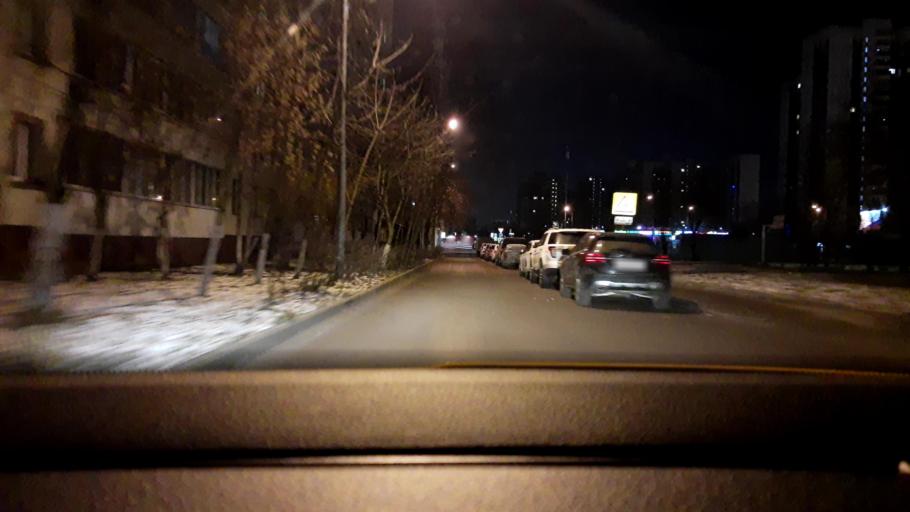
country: RU
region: Moscow
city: Lianozovo
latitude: 55.8996
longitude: 37.5916
